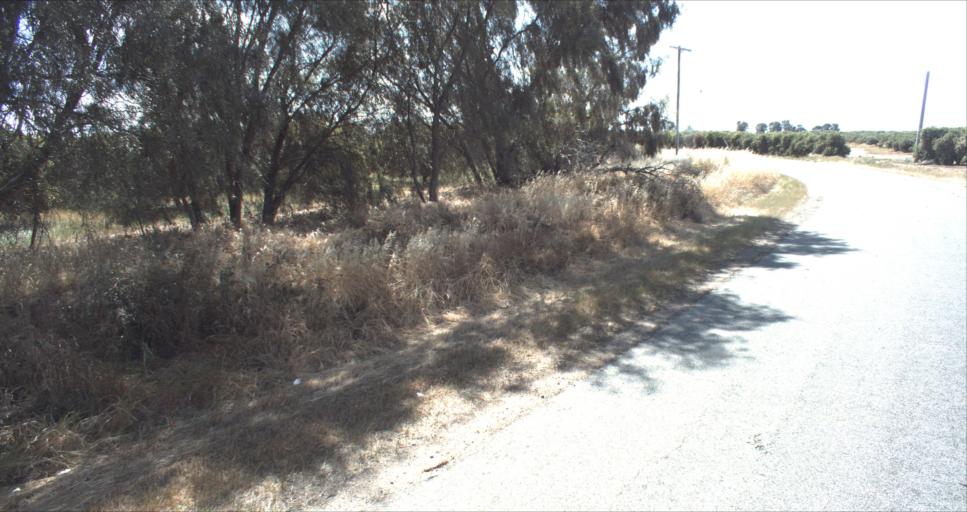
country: AU
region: New South Wales
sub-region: Leeton
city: Leeton
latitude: -34.5088
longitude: 146.2244
